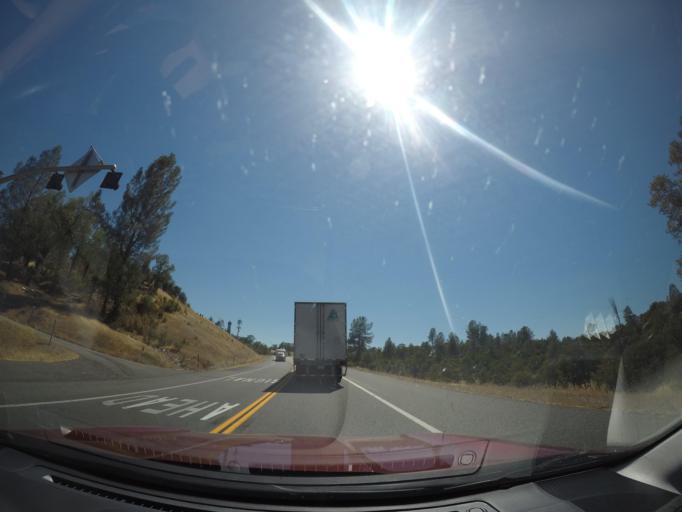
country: US
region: California
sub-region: Shasta County
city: Bella Vista
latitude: 40.6372
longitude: -122.2479
